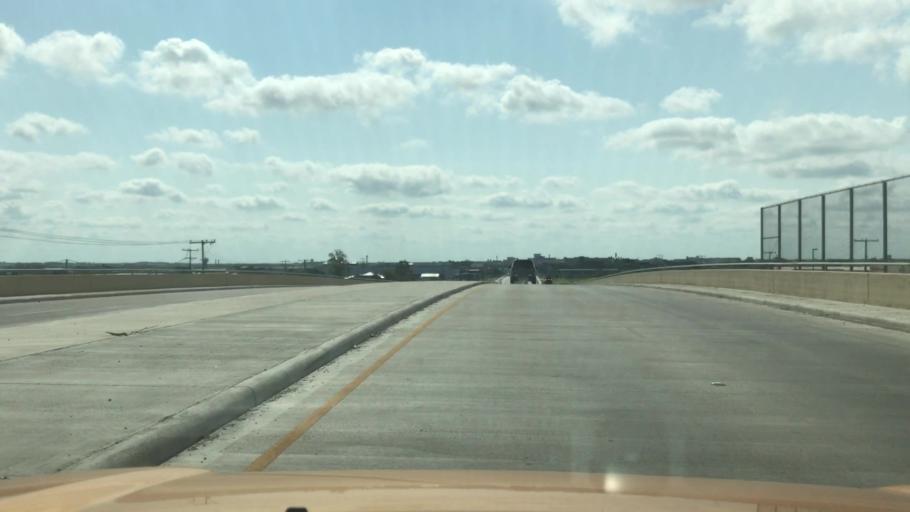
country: US
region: Texas
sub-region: Comal County
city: New Braunfels
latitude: 29.7377
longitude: -98.0886
